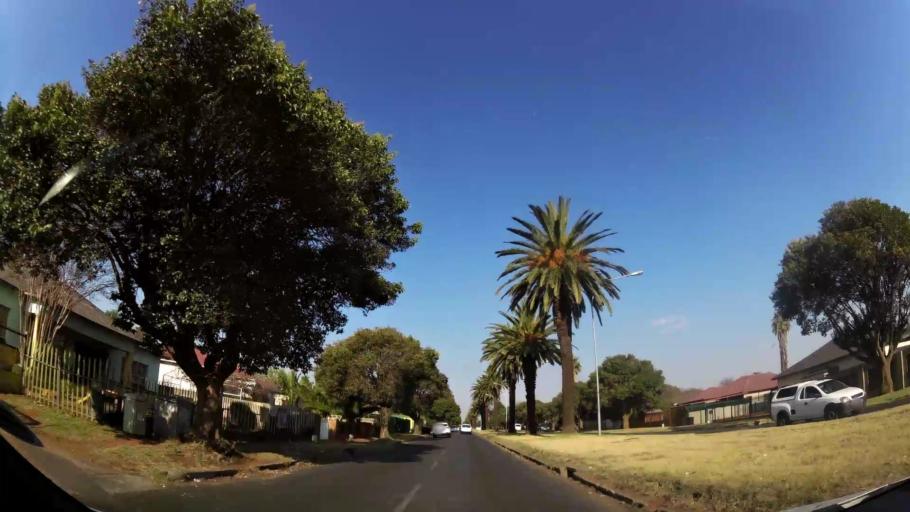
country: ZA
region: Gauteng
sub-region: Ekurhuleni Metropolitan Municipality
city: Brakpan
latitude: -26.2470
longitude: 28.3707
